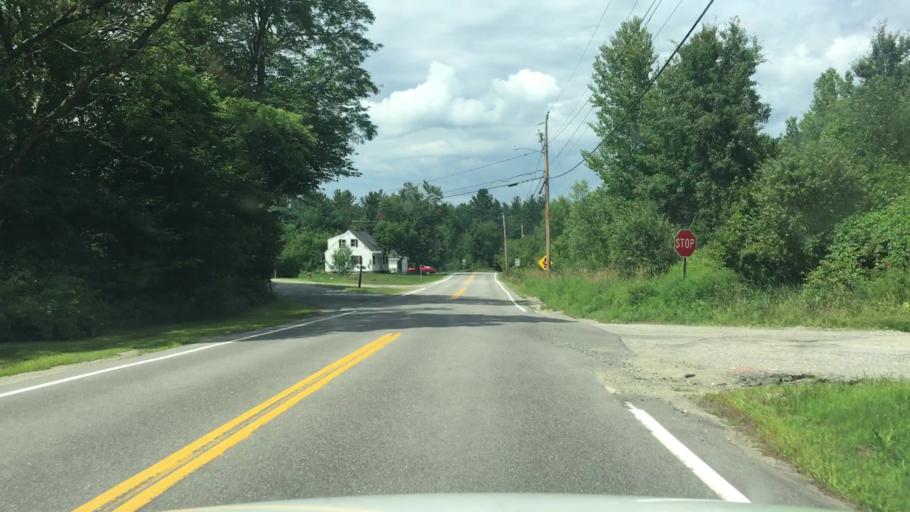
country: US
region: New Hampshire
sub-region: Grafton County
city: Deerfield
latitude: 44.2954
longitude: -71.6586
